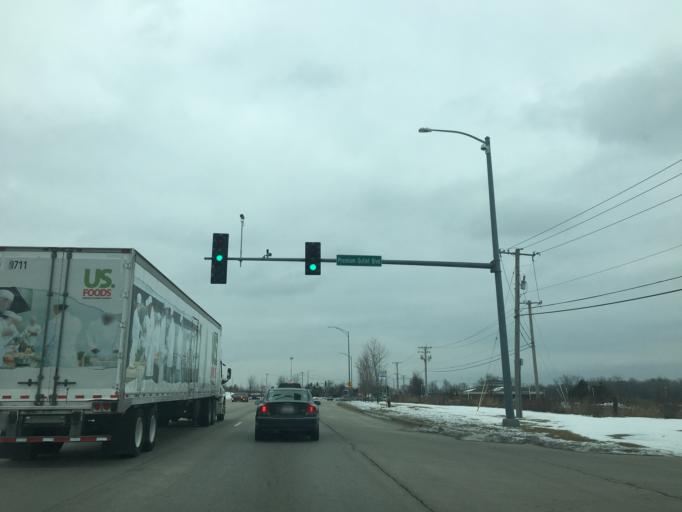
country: US
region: Illinois
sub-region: Kane County
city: North Aurora
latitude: 41.8040
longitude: -88.2821
